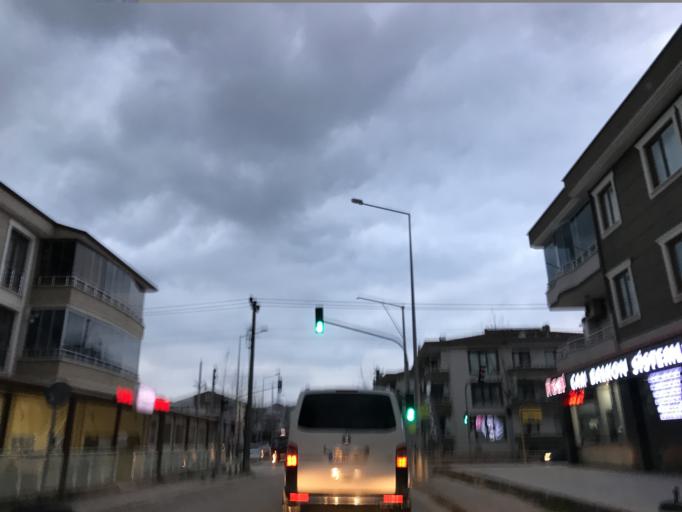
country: TR
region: Yalova
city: Yalova
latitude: 40.6413
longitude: 29.2589
